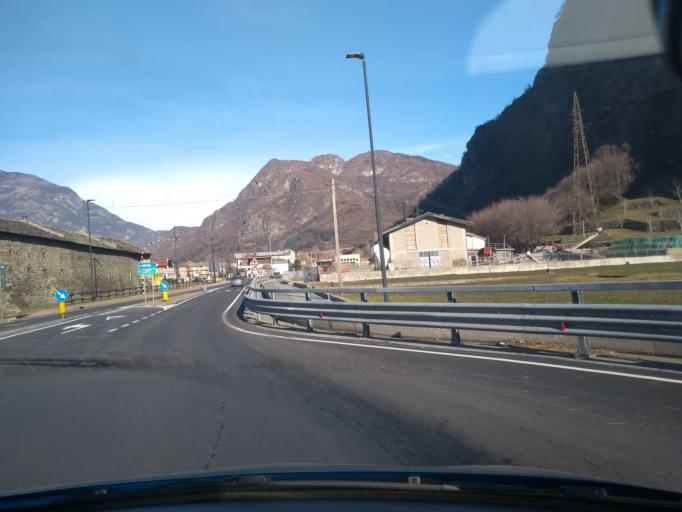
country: IT
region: Aosta Valley
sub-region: Valle d'Aosta
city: Verres
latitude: 45.6587
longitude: 7.6948
